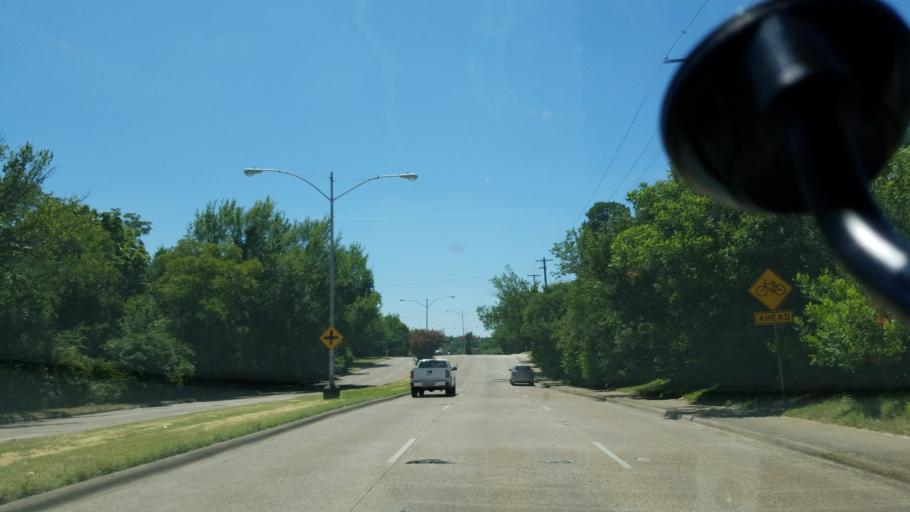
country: US
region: Texas
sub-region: Dallas County
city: Cockrell Hill
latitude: 32.7058
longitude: -96.8530
